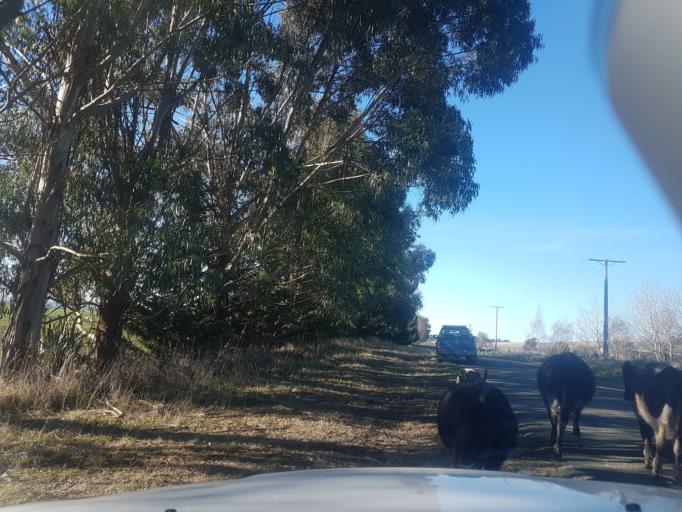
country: NZ
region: Canterbury
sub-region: Timaru District
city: Pleasant Point
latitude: -44.2907
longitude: 171.0643
